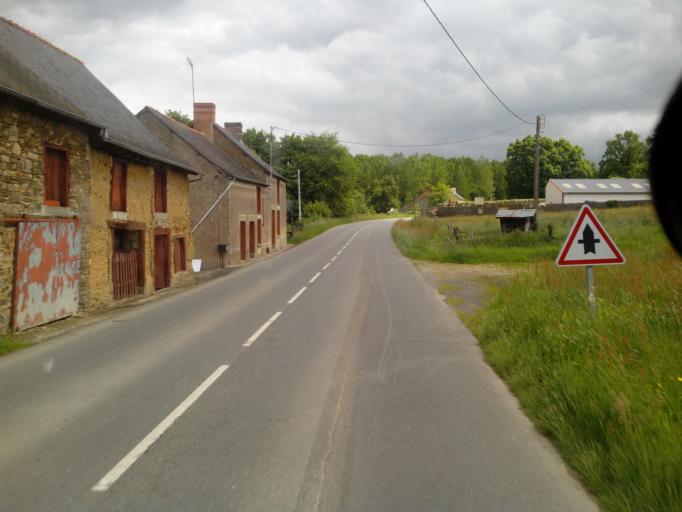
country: FR
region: Brittany
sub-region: Departement d'Ille-et-Vilaine
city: Chasne-sur-Illet
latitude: 48.2465
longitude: -1.5727
